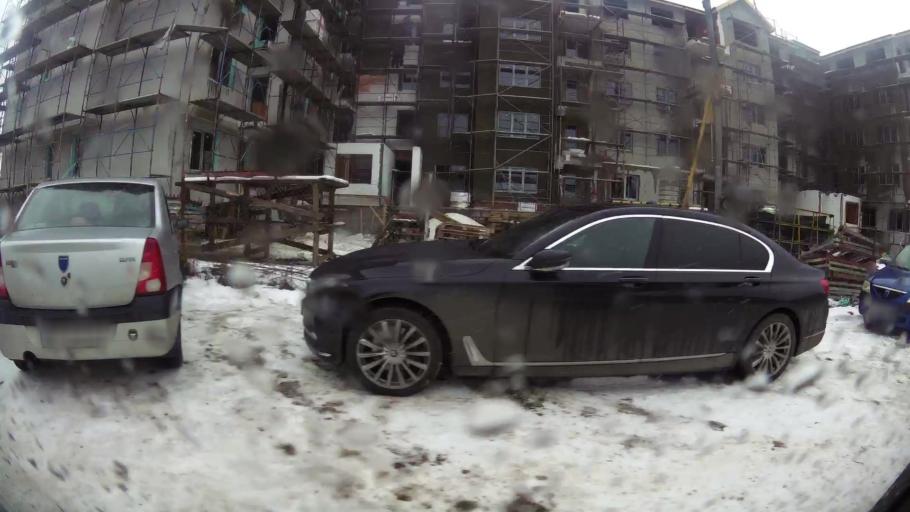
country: RO
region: Ilfov
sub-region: Comuna Chiajna
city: Rosu
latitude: 44.4175
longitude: 26.0052
